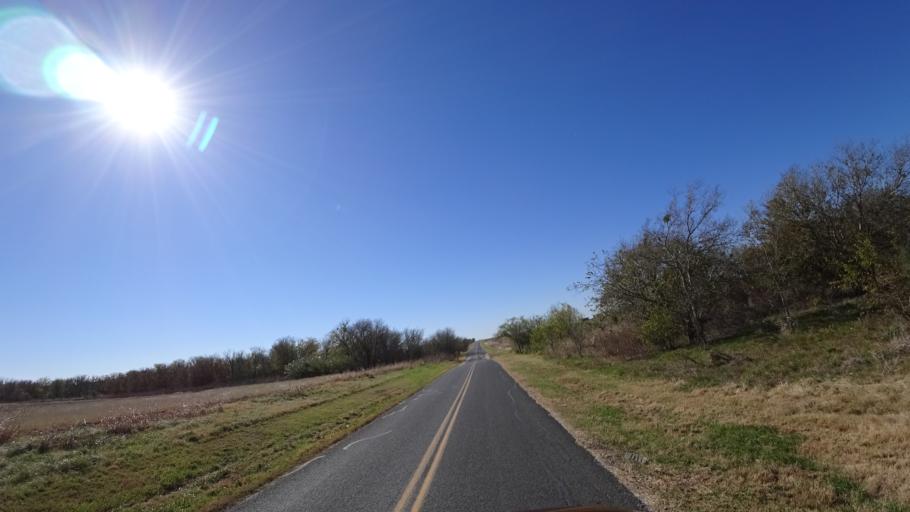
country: US
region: Texas
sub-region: Travis County
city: Garfield
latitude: 30.0951
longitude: -97.6201
